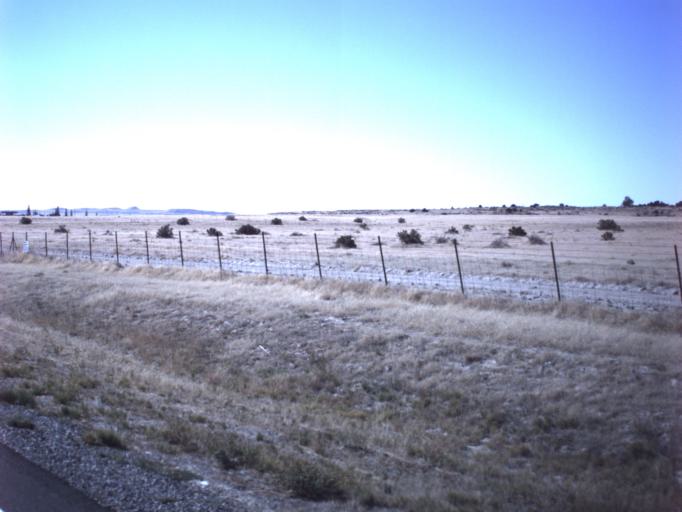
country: US
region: Utah
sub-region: Tooele County
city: Grantsville
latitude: 40.2381
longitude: -112.7232
